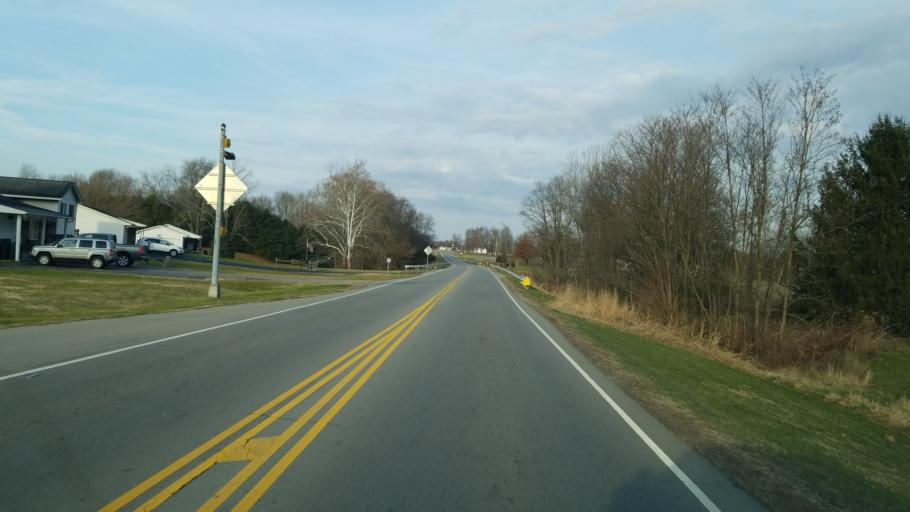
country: US
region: Ohio
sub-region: Ross County
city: Chillicothe
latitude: 39.2883
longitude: -82.8696
